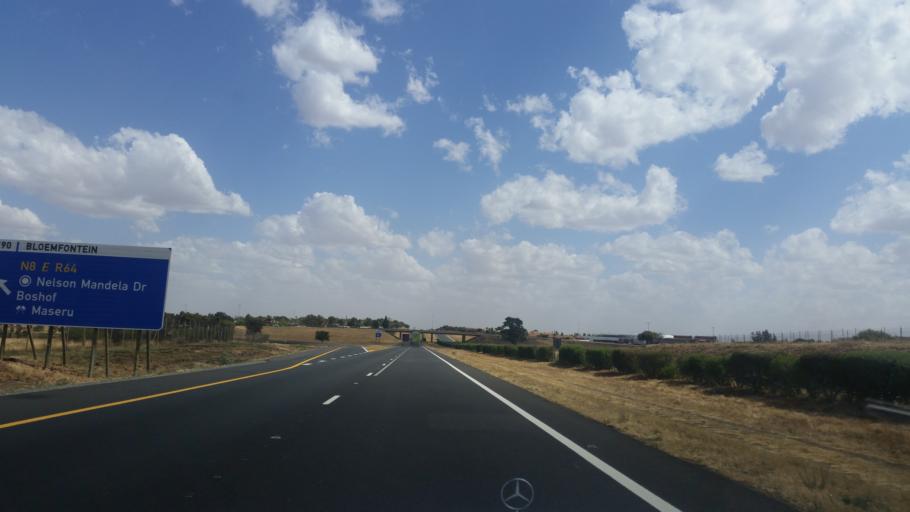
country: ZA
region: Orange Free State
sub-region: Mangaung Metropolitan Municipality
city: Bloemfontein
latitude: -29.0864
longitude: 26.1740
